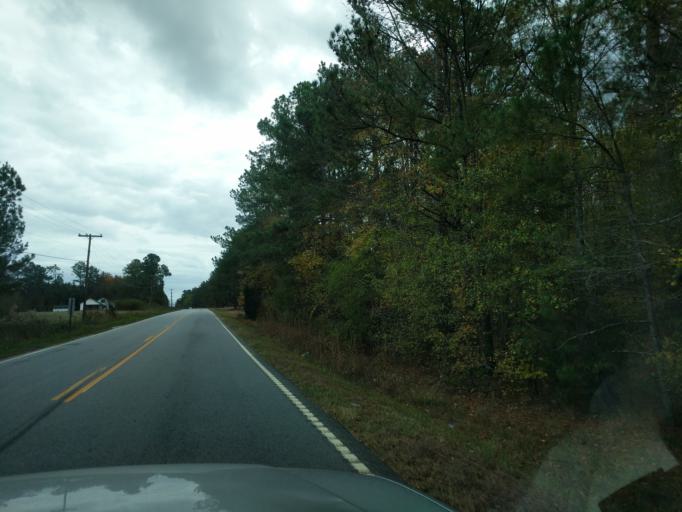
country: US
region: South Carolina
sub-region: Saluda County
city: Saluda
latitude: 34.0208
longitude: -81.7895
